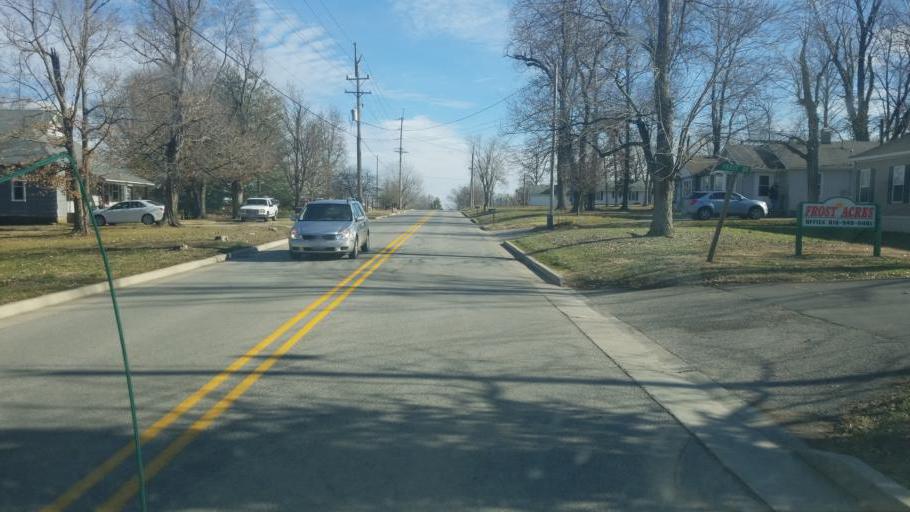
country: US
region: Illinois
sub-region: Jackson County
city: Carbondale
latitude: 37.7003
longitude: -89.2061
